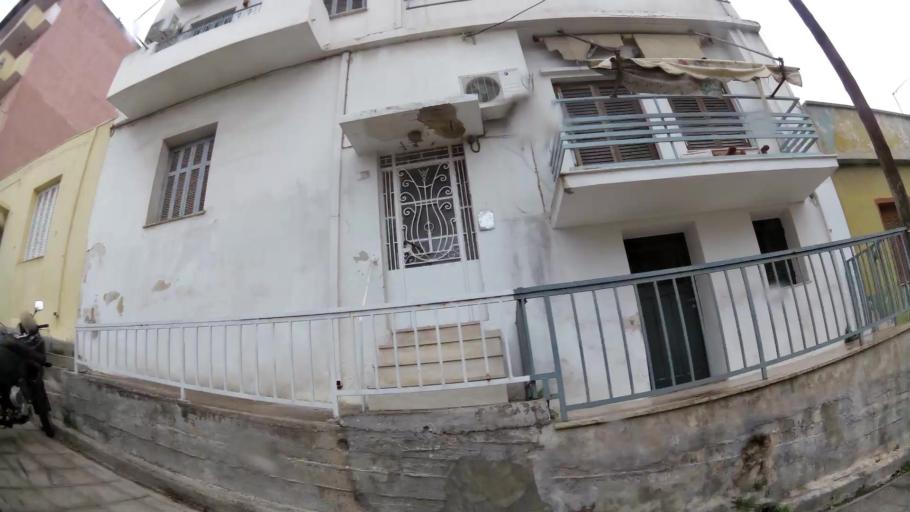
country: GR
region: Attica
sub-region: Nomos Piraios
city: Nikaia
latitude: 37.9606
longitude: 23.6455
